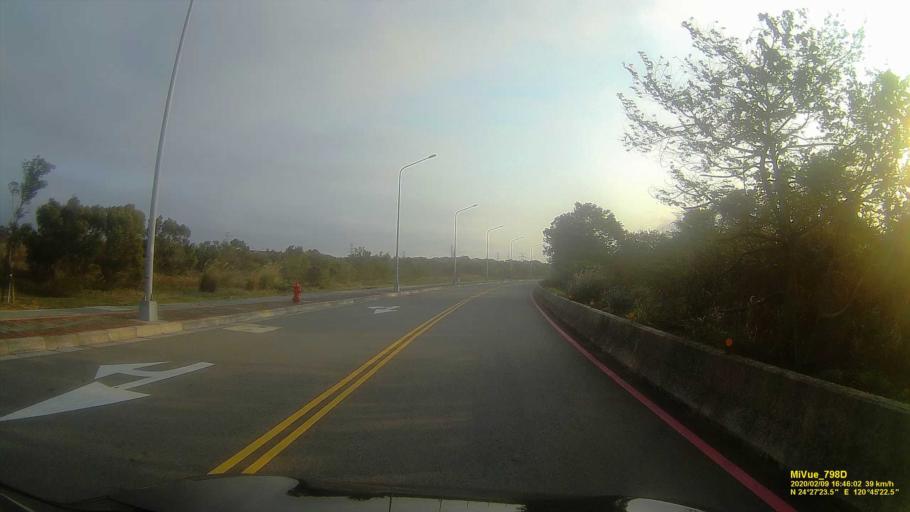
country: TW
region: Taiwan
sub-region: Miaoli
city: Miaoli
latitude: 24.4563
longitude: 120.7562
